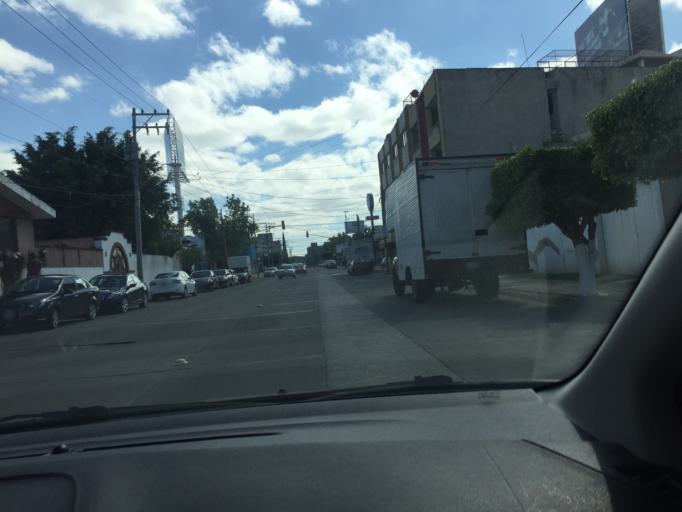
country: MX
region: Guanajuato
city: Leon
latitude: 21.1515
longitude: -101.6903
